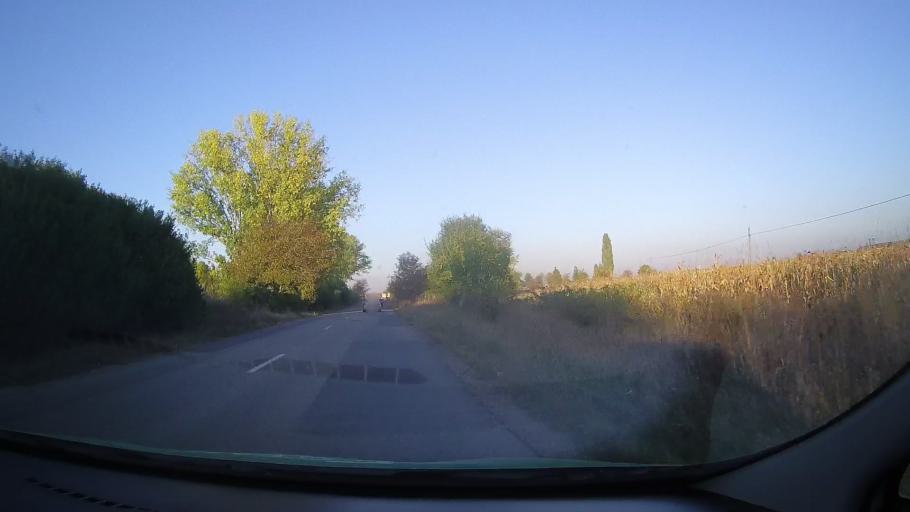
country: RO
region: Bihor
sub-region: Comuna Salard
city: Salard
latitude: 47.2087
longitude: 22.0193
